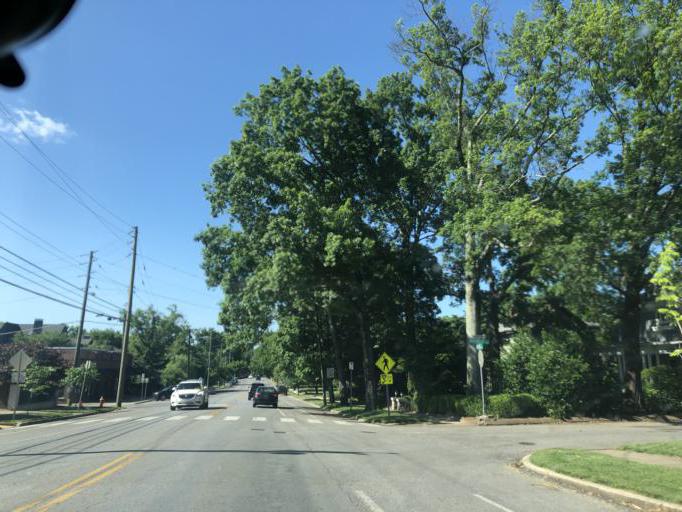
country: US
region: Tennessee
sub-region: Davidson County
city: Oak Hill
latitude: 36.1239
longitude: -86.7945
